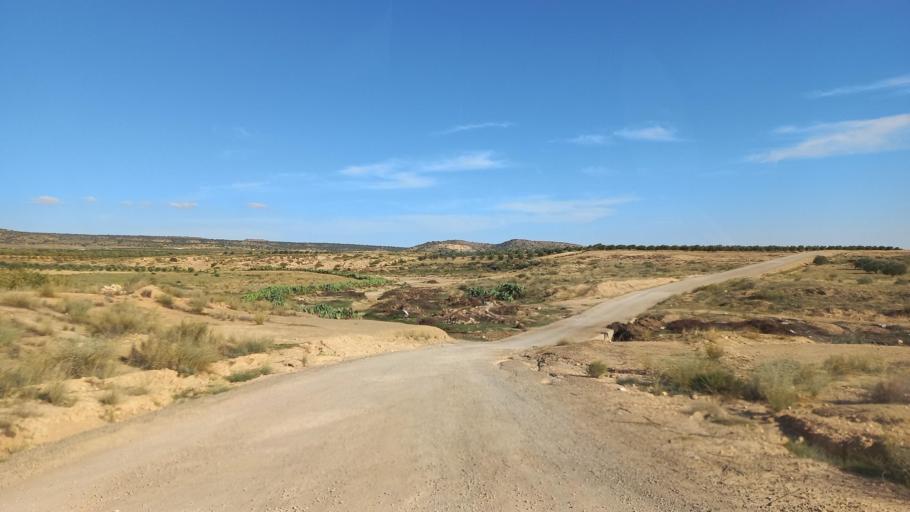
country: TN
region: Al Qasrayn
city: Sbiba
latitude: 35.3016
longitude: 9.0946
